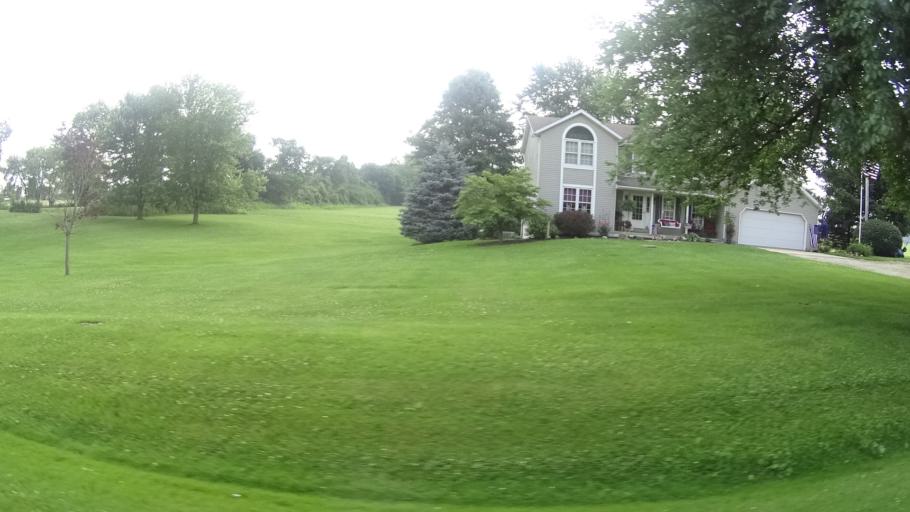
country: US
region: Ohio
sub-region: Huron County
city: Wakeman
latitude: 41.3174
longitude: -82.4136
